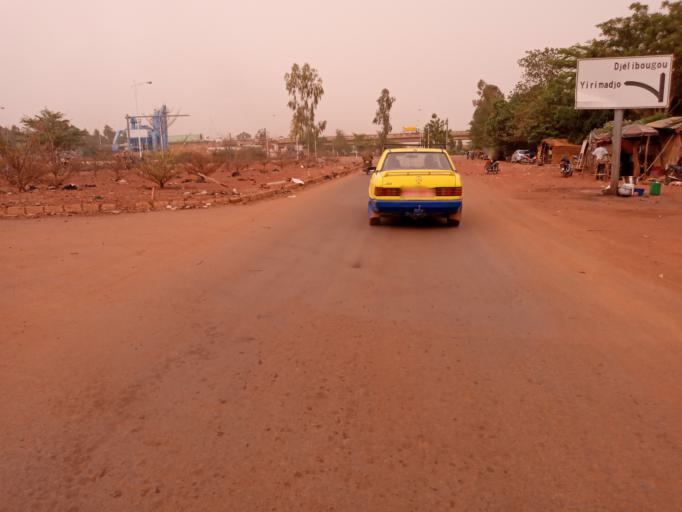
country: ML
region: Bamako
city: Bamako
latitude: 12.6483
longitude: -7.9312
